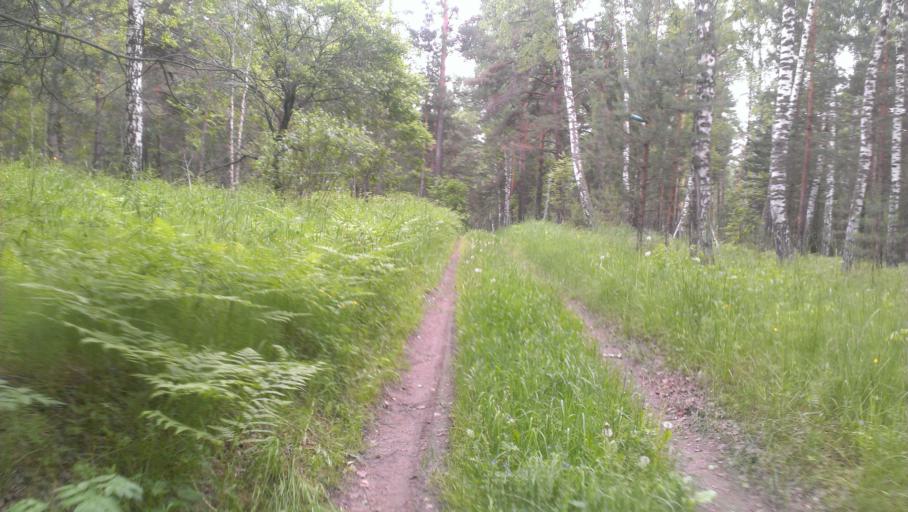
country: RU
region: Altai Krai
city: Sannikovo
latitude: 53.3435
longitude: 84.0446
